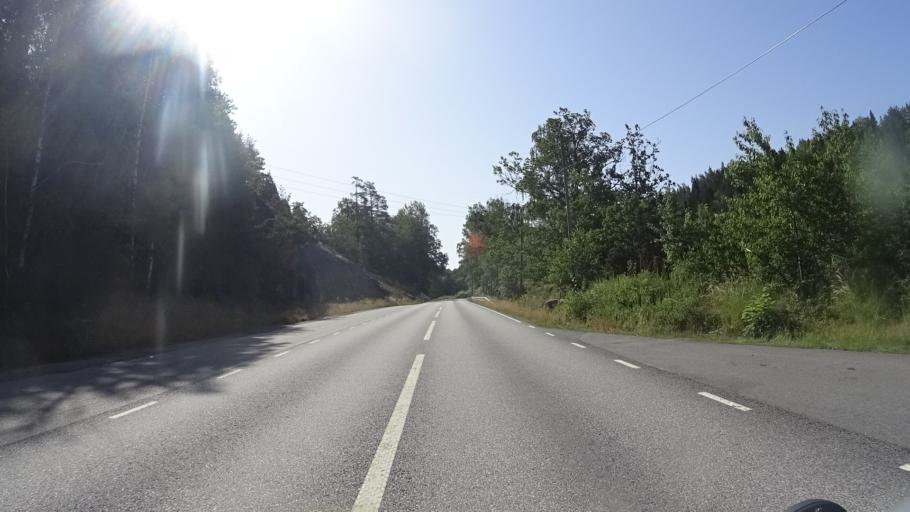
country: SE
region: Kalmar
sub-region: Vasterviks Kommun
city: Overum
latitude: 58.0190
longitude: 16.2498
